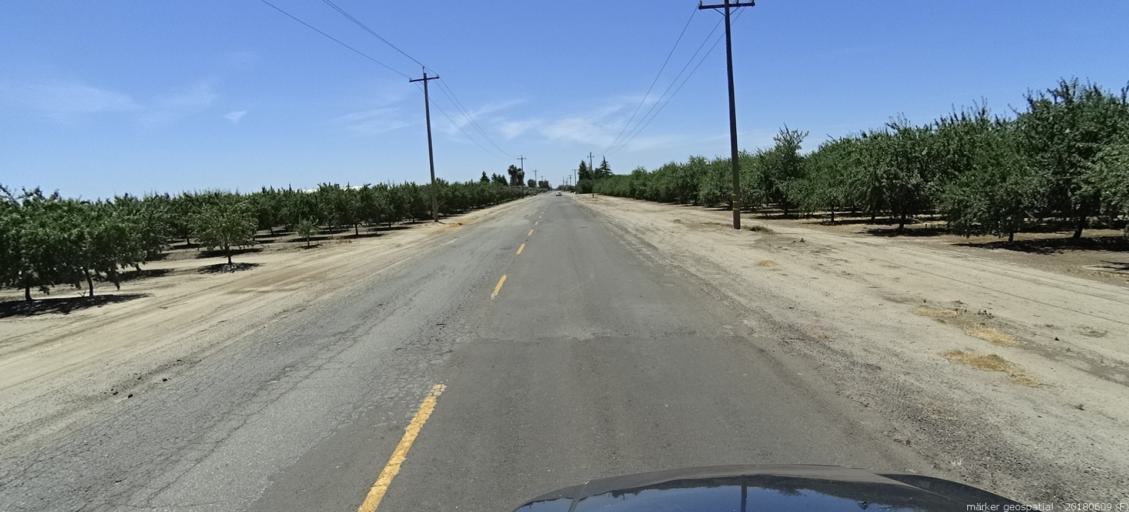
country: US
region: California
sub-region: Madera County
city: Parkwood
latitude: 36.9296
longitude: -120.0652
